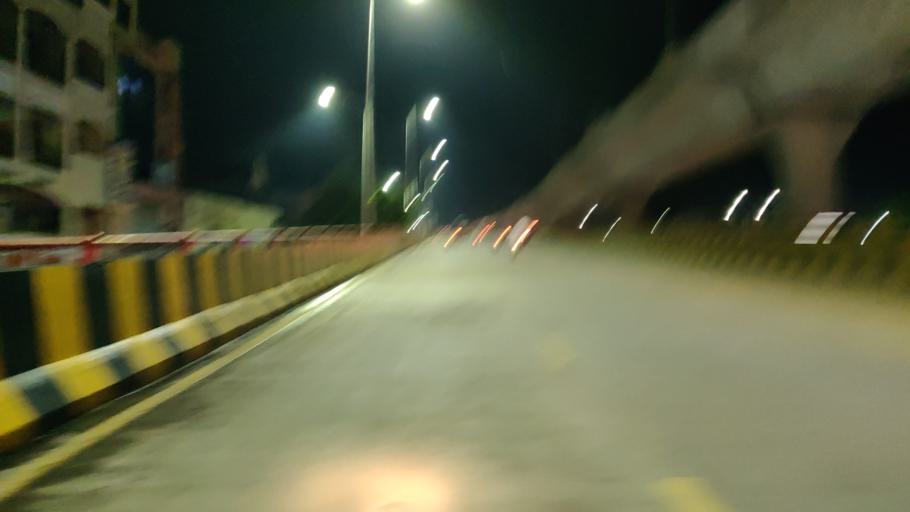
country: IN
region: Telangana
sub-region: Rangareddi
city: Lal Bahadur Nagar
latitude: 17.3485
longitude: 78.5492
